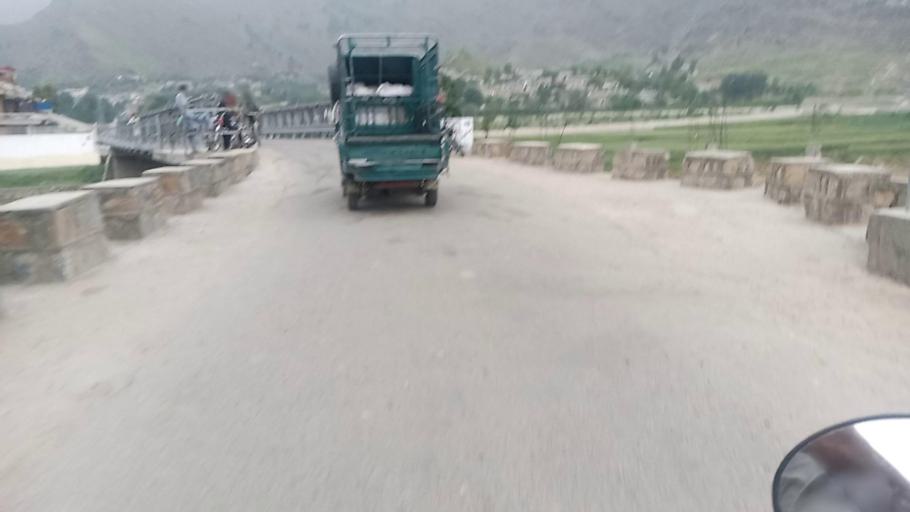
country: PK
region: Khyber Pakhtunkhwa
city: Mingora
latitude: 34.7692
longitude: 72.3720
